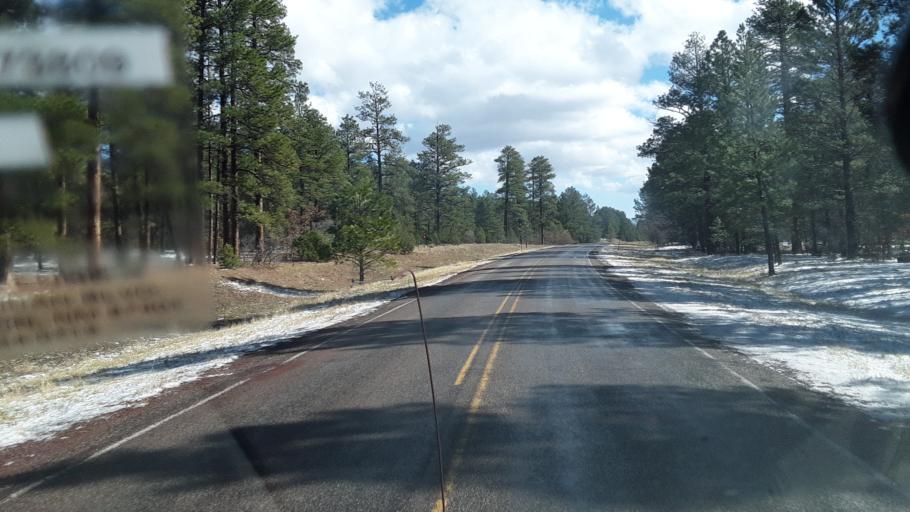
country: US
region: New Mexico
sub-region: Rio Arriba County
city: Santa Teresa
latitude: 36.2003
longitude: -106.7627
